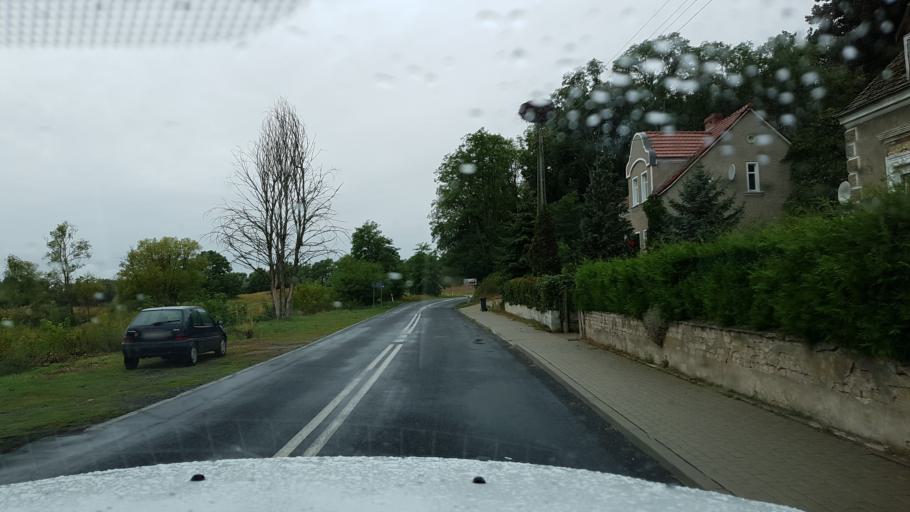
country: PL
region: West Pomeranian Voivodeship
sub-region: Powiat gryfinski
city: Cedynia
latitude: 52.8320
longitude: 14.1786
